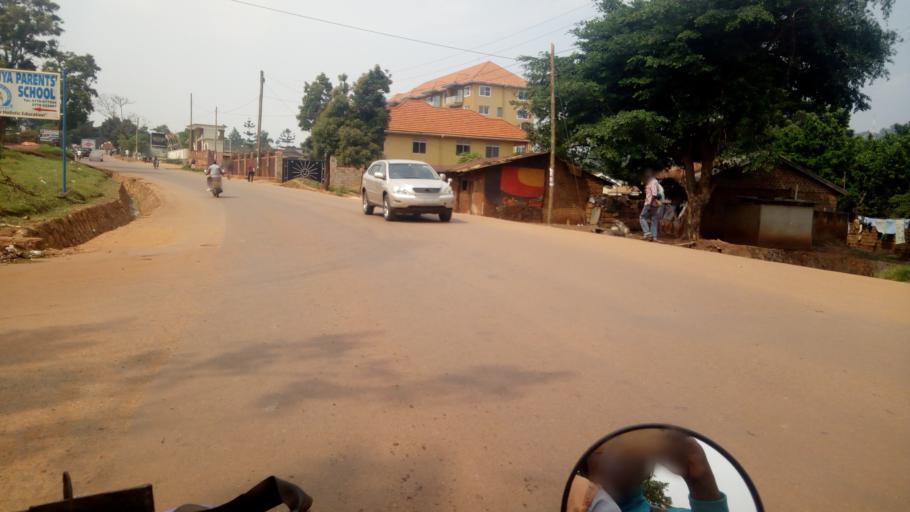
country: UG
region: Central Region
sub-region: Wakiso District
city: Kireka
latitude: 0.3192
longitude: 32.6329
